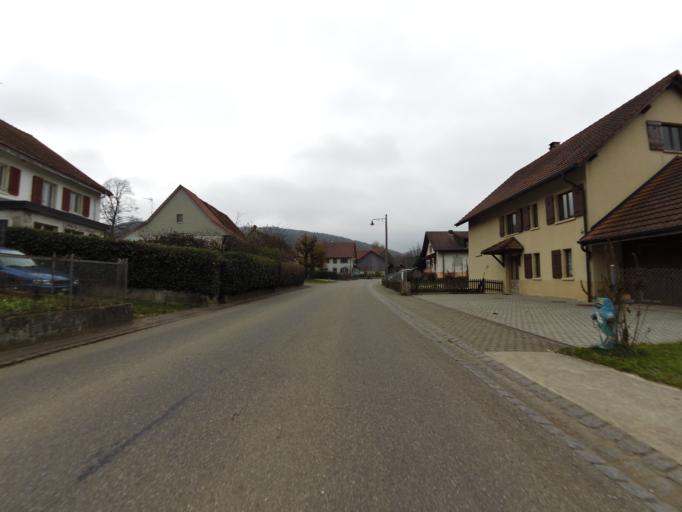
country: CH
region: Jura
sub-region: Porrentruy District
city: Alle
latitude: 47.4238
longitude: 7.2084
